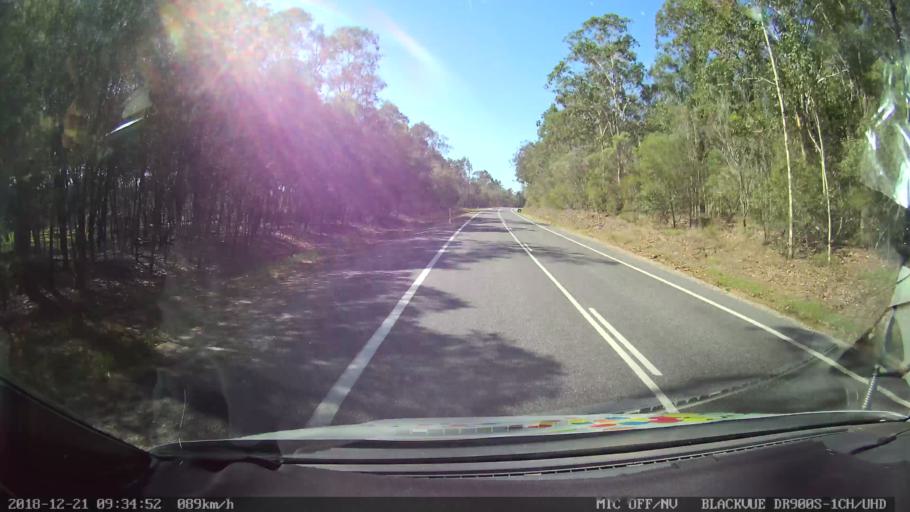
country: AU
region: New South Wales
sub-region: Clarence Valley
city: Grafton
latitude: -29.5034
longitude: 152.9819
